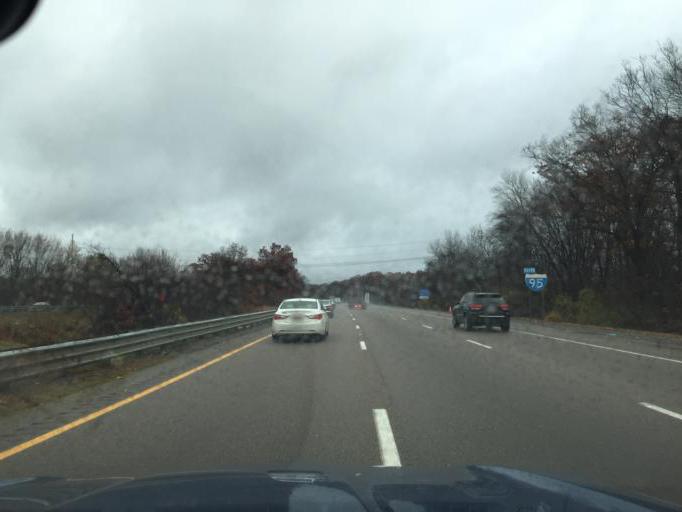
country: US
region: Massachusetts
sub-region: Bristol County
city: North Seekonk
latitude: 41.9061
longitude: -71.3451
